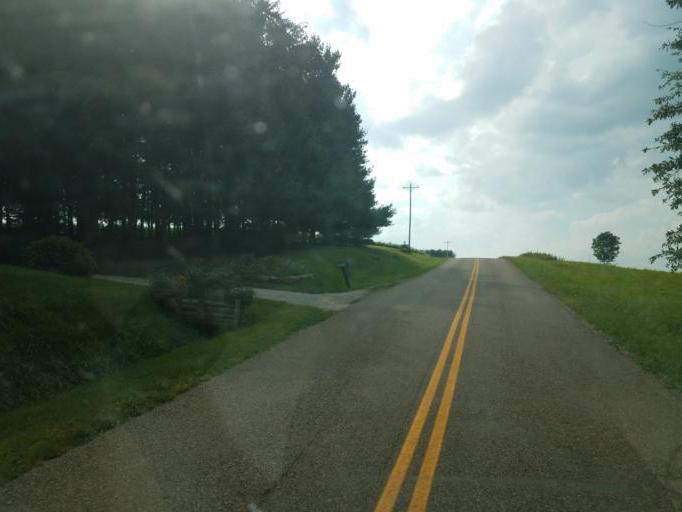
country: US
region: Ohio
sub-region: Knox County
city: Gambier
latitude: 40.3365
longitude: -82.3630
